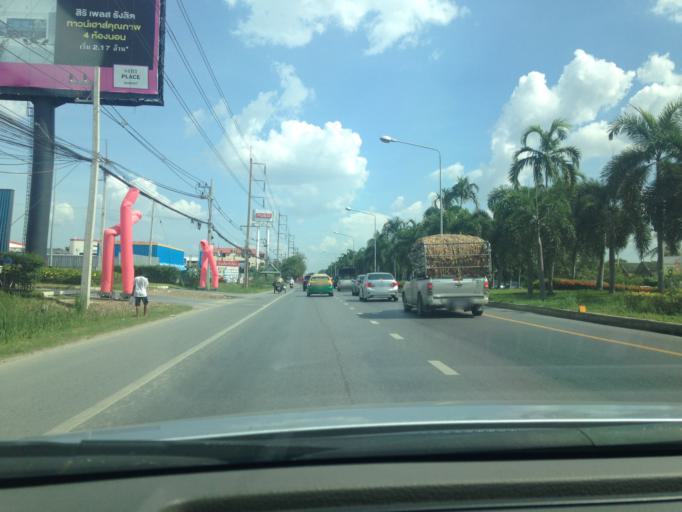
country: TH
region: Phra Nakhon Si Ayutthaya
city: Ban Bang Kadi Pathum Thani
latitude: 13.9979
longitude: 100.5735
